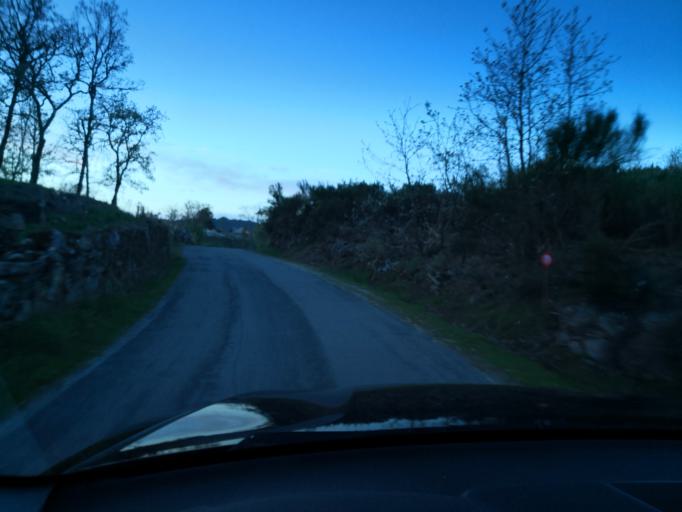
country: PT
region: Vila Real
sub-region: Vila Real
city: Vila Real
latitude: 41.3659
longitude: -7.6547
